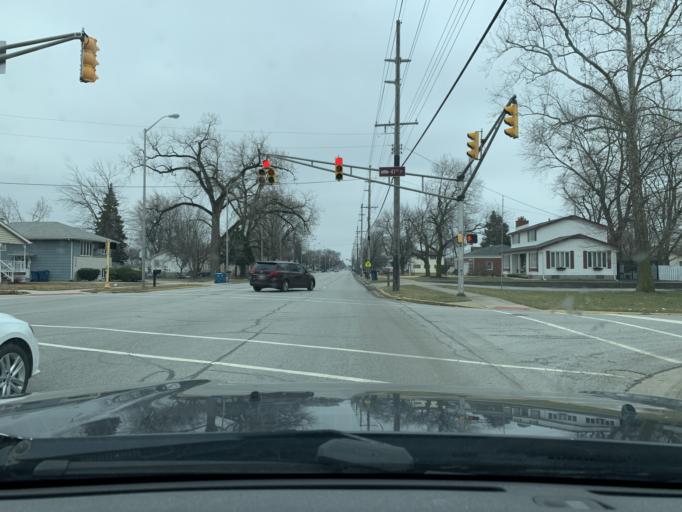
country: US
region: Indiana
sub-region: Lake County
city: Highland
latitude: 41.5450
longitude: -87.4616
